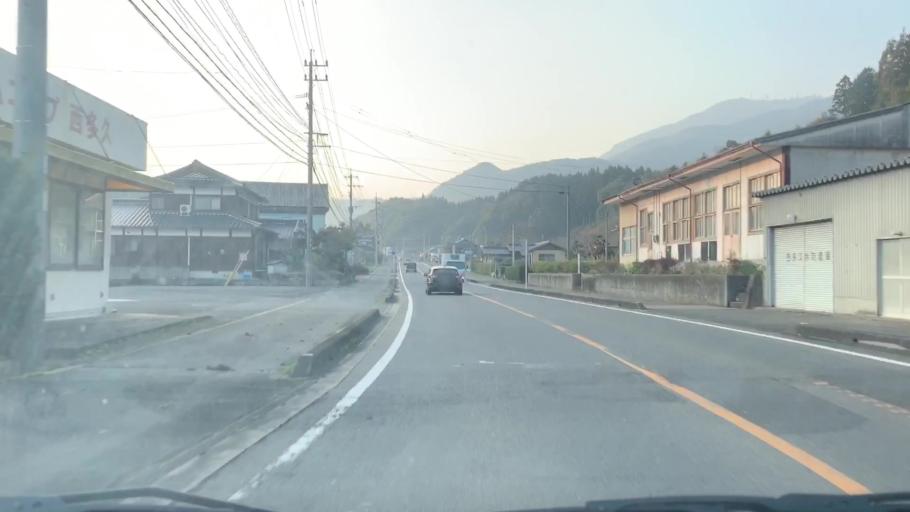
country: JP
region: Saga Prefecture
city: Takeocho-takeo
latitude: 33.2633
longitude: 130.0563
